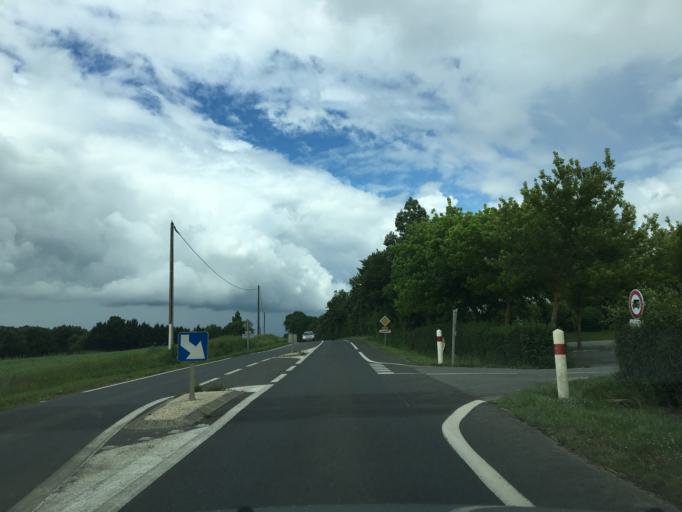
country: FR
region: Poitou-Charentes
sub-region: Departement de la Charente-Maritime
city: Saint-Jean-d'Angely
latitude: 46.0518
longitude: -0.5106
